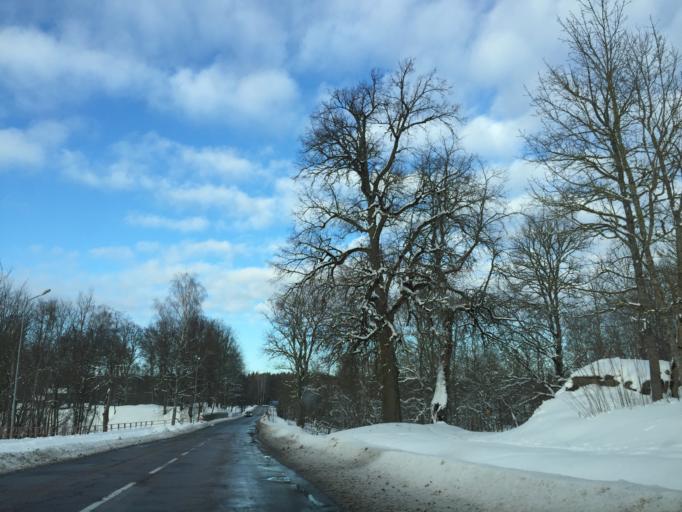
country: LV
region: Ropazu
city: Ropazi
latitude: 56.9771
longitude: 24.6318
